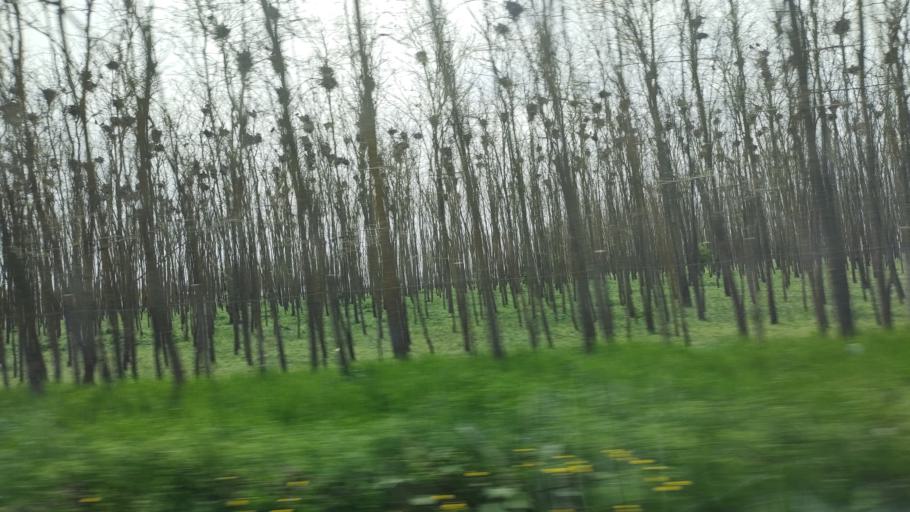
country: RO
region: Constanta
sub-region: Comuna Cobadin
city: Viisoara
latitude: 44.0780
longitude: 28.1759
